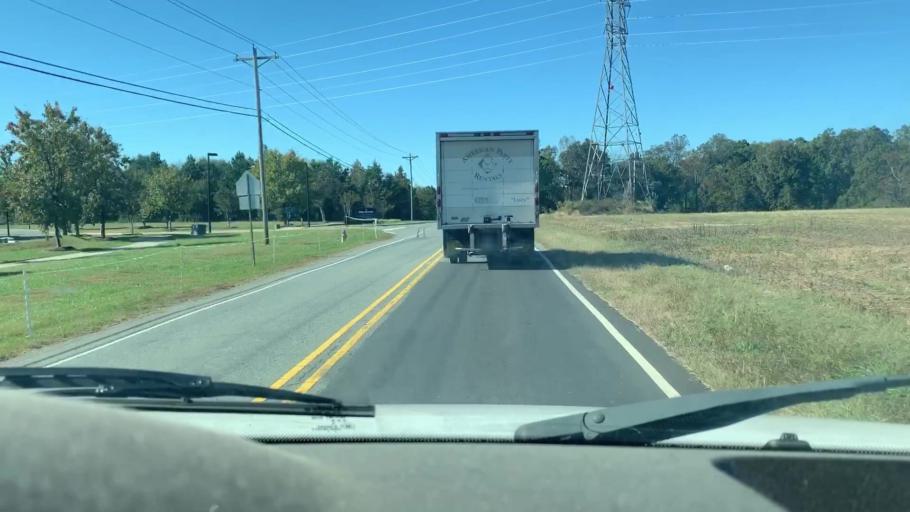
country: US
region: North Carolina
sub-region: Mecklenburg County
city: Cornelius
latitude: 35.4669
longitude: -80.8424
